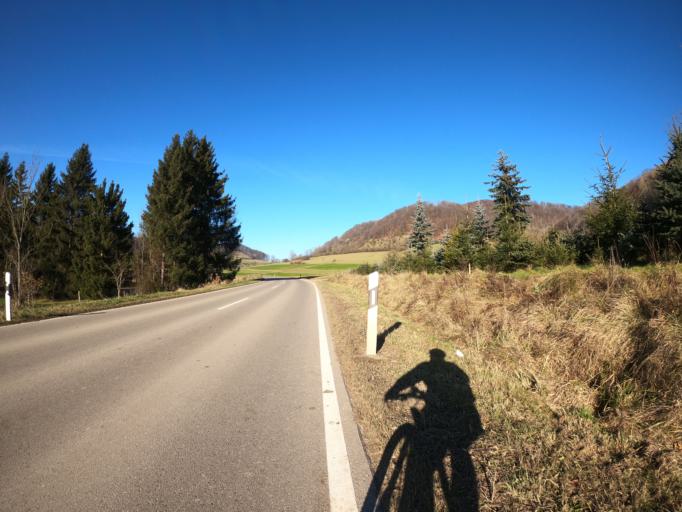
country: DE
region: Baden-Wuerttemberg
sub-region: Regierungsbezirk Stuttgart
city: Eschenbach
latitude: 48.6200
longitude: 9.6790
